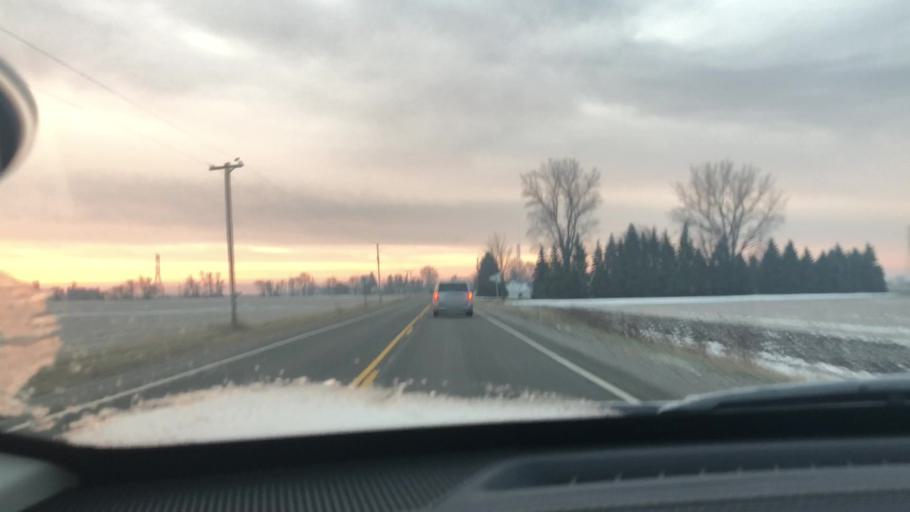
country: US
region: Michigan
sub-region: Saginaw County
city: Zilwaukee
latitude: 43.5059
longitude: -83.8361
